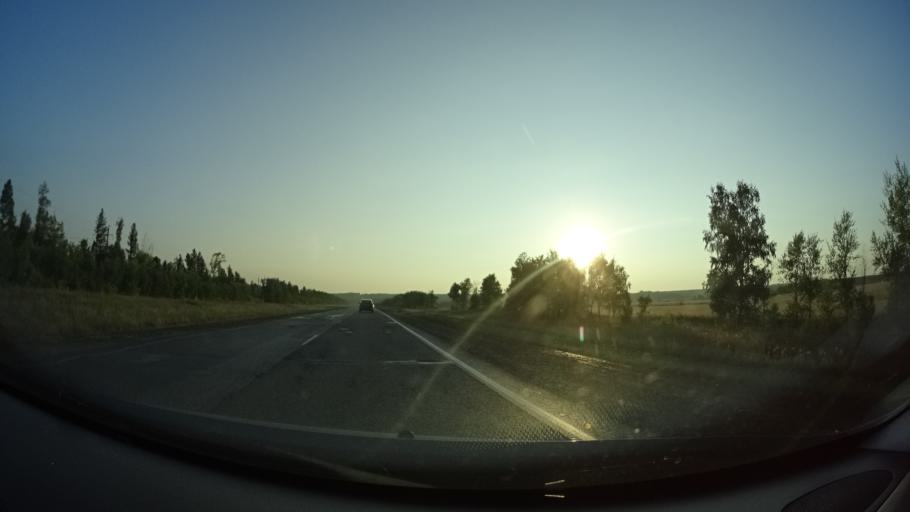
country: RU
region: Samara
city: Isakly
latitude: 54.0042
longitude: 51.5879
